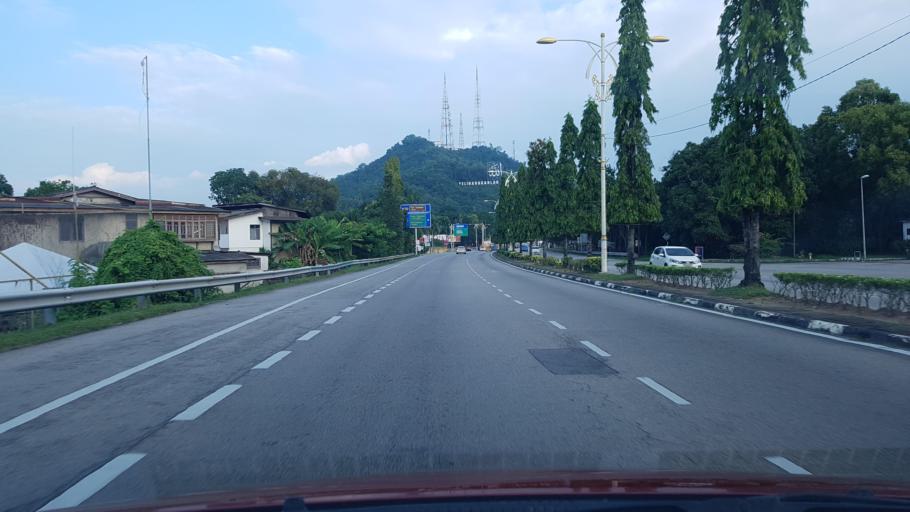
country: MY
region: Terengganu
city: Kuala Terengganu
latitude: 5.3159
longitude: 103.1298
